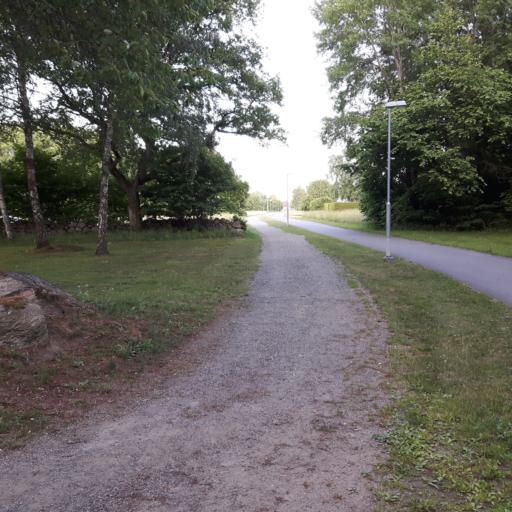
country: SE
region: Skane
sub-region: Hassleholms Kommun
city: Vinslov
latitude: 56.0931
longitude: 13.9020
